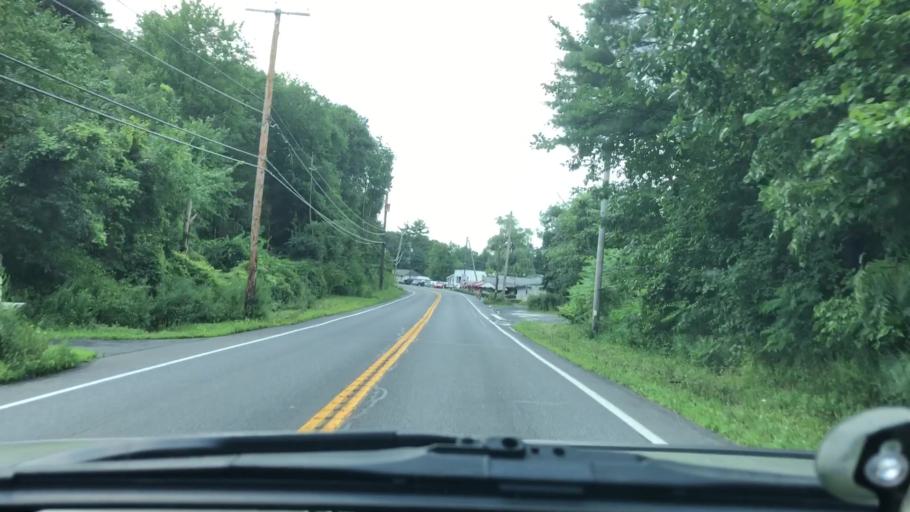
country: US
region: New York
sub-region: Ulster County
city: Manorville
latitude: 42.1371
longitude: -74.0013
